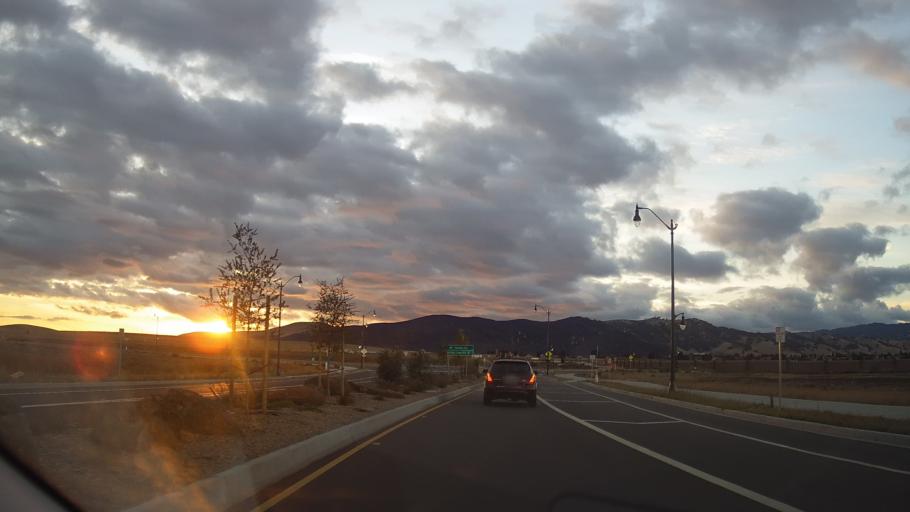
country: US
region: California
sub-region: Solano County
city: Vacaville
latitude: 38.3173
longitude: -121.9414
